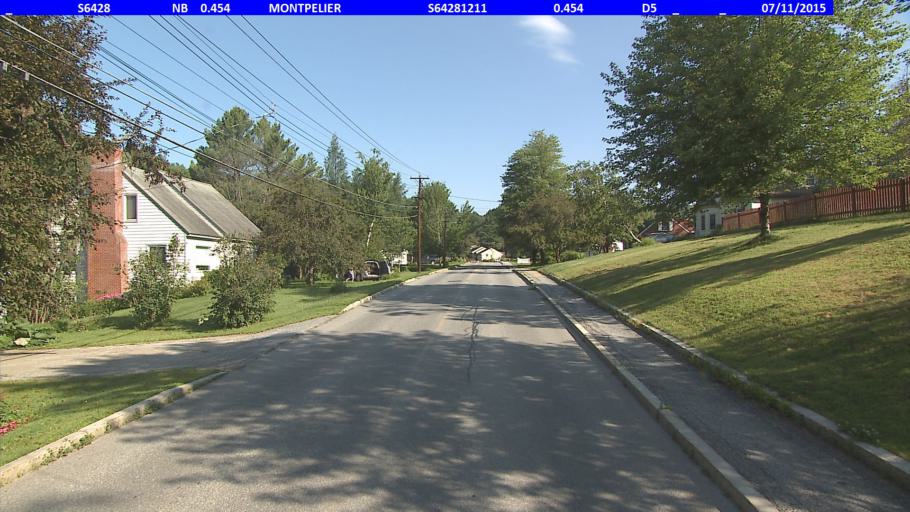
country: US
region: Vermont
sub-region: Washington County
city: Montpelier
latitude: 44.2691
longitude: -72.5886
